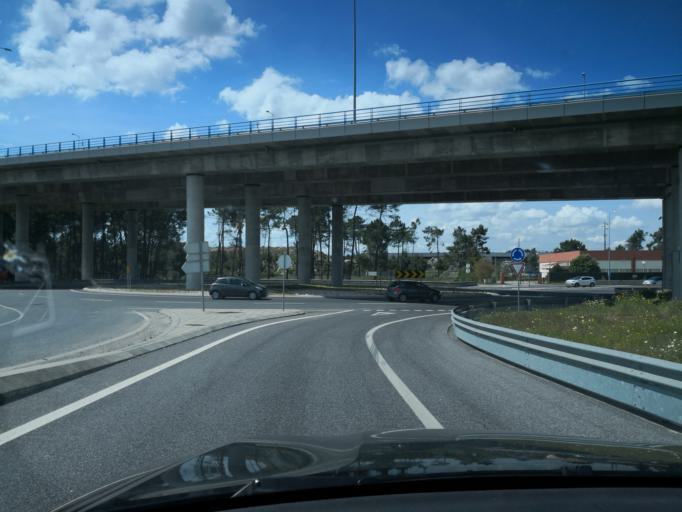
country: PT
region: Setubal
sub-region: Seixal
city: Aldeia de Paio Pires
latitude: 38.5934
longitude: -9.0535
